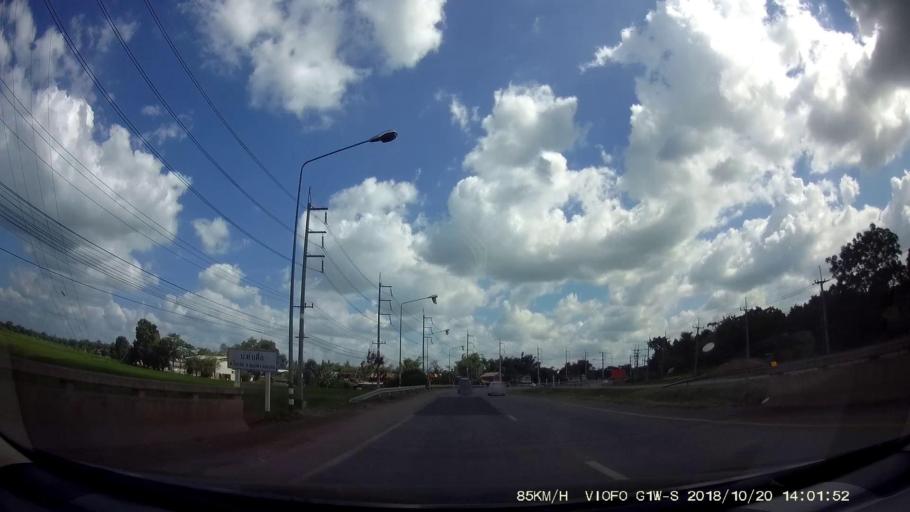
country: TH
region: Khon Kaen
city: Chum Phae
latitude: 16.4978
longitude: 102.1240
